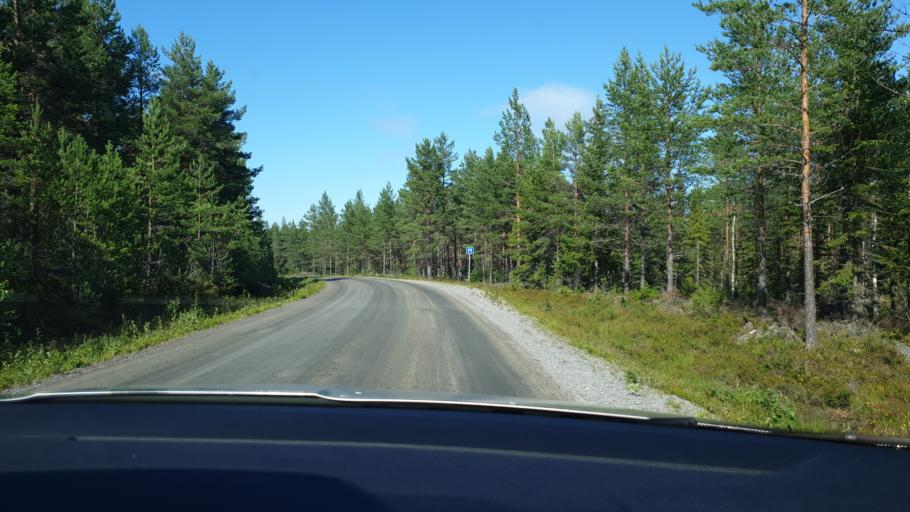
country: SE
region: Gaevleborg
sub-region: Soderhamns Kommun
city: Soderhamn
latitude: 61.4342
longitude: 17.0066
